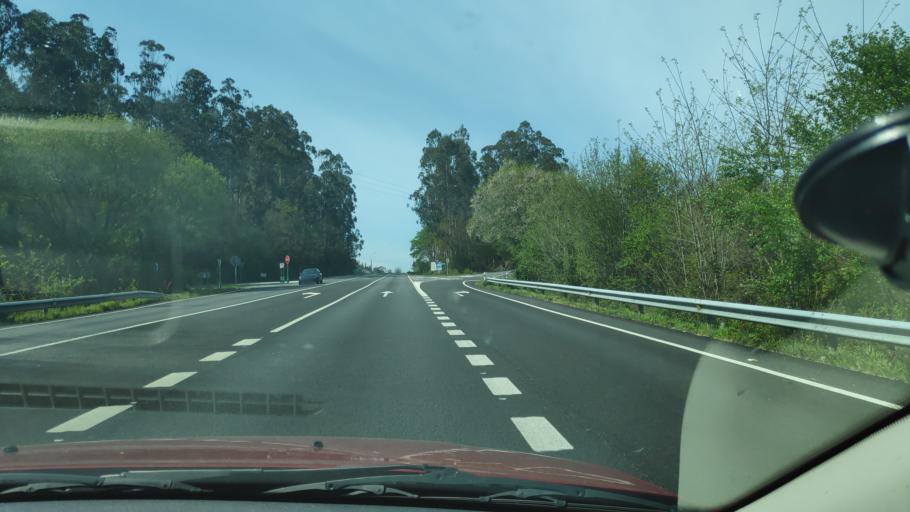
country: ES
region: Galicia
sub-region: Provincia da Coruna
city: Ames
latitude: 42.8779
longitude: -8.6754
